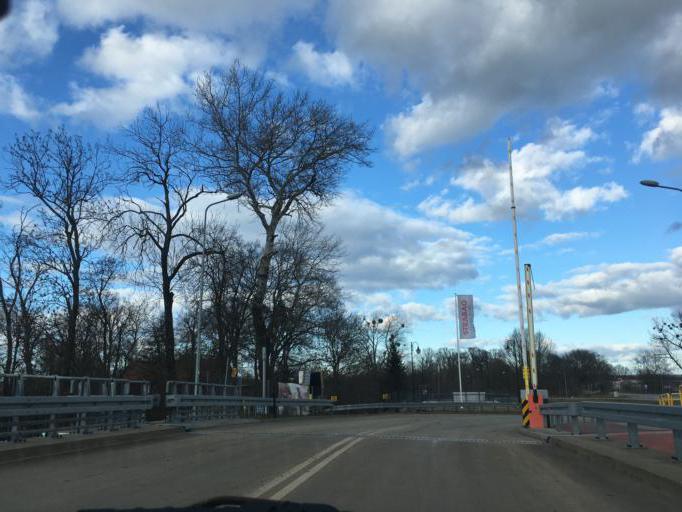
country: PL
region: Pomeranian Voivodeship
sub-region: Powiat gdanski
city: Cedry Wielkie
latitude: 54.3087
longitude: 18.9234
